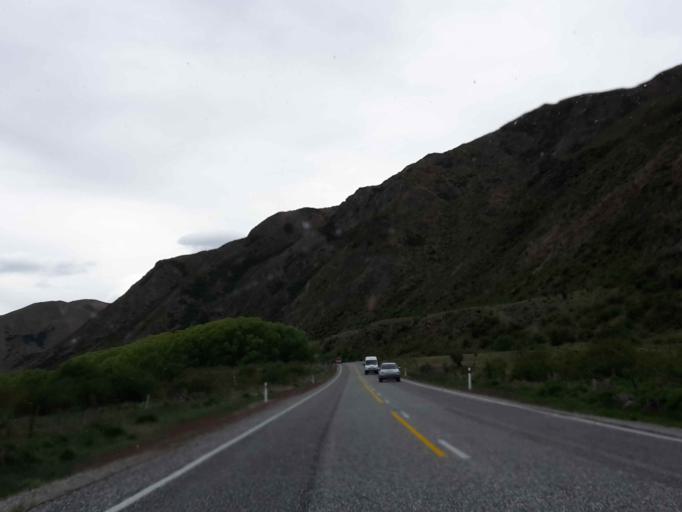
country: NZ
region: Otago
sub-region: Queenstown-Lakes District
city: Wanaka
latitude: -44.6259
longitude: 169.5221
